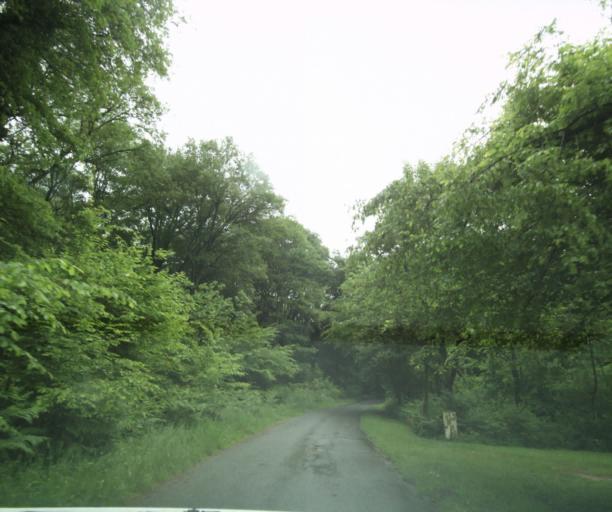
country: FR
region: Bourgogne
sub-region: Departement de Saone-et-Loire
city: Ciry-le-Noble
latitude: 46.5210
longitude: 4.3020
